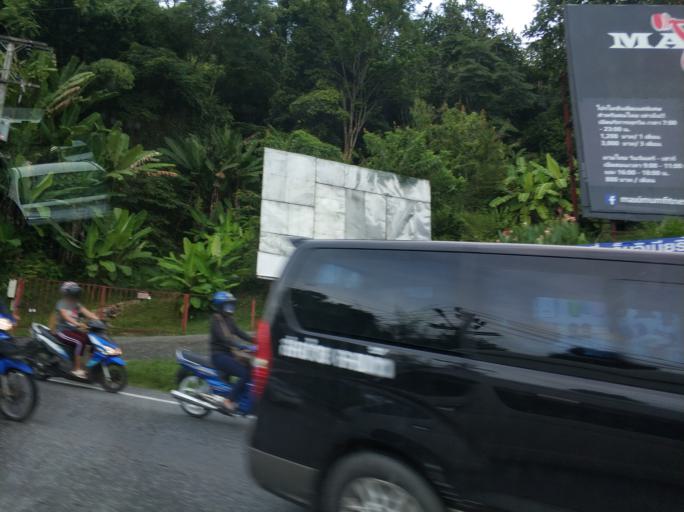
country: TH
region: Phuket
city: Kathu
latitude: 7.9053
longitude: 98.3230
